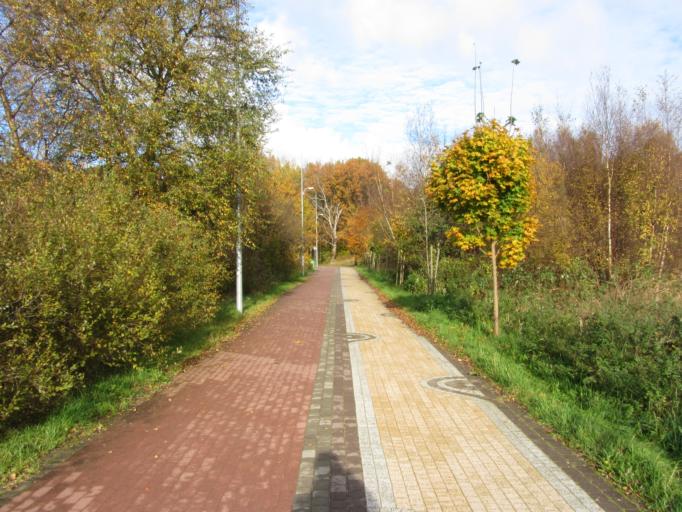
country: PL
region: West Pomeranian Voivodeship
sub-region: Powiat kolobrzeski
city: Grzybowo
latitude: 54.1725
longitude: 15.5278
